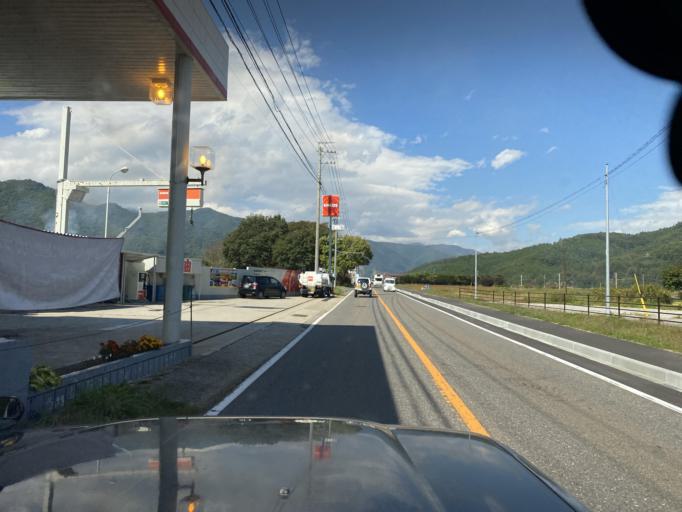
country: JP
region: Nagano
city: Omachi
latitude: 36.5301
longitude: 137.8482
